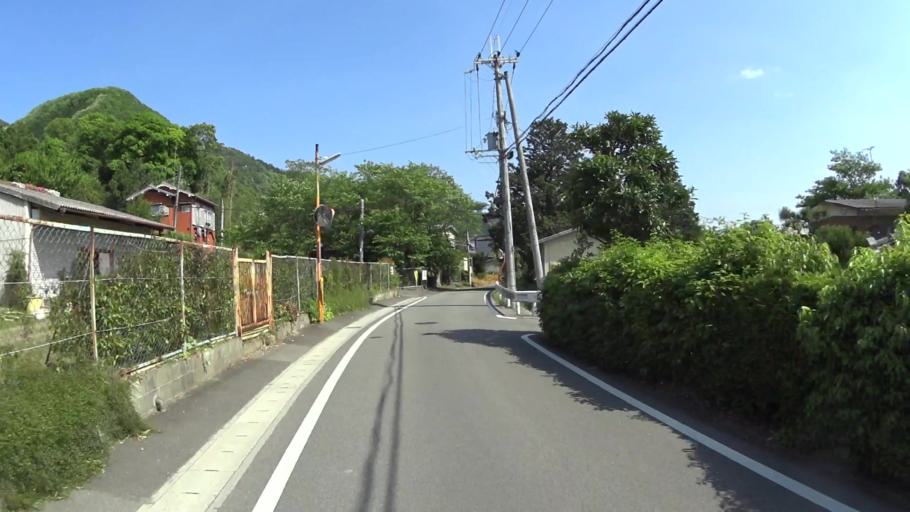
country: JP
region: Kyoto
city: Kameoka
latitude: 35.0620
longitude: 135.5752
